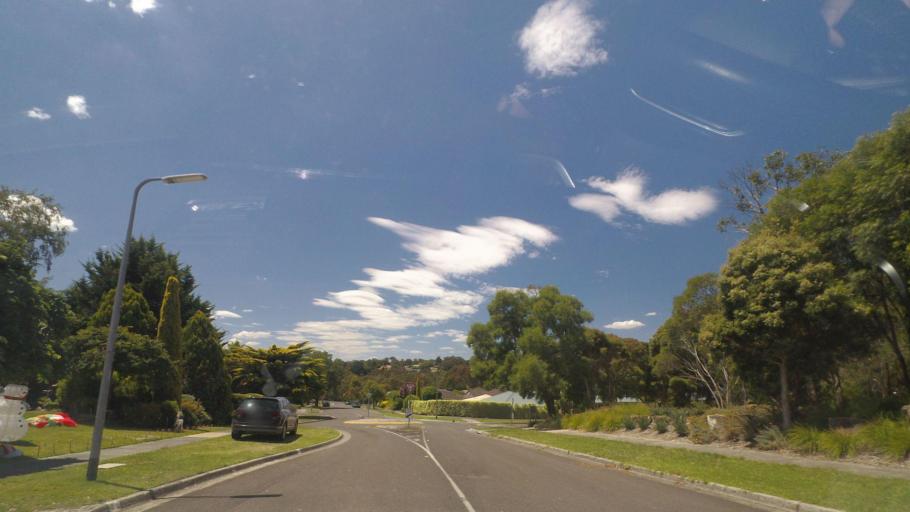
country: AU
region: Victoria
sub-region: Yarra Ranges
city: Kilsyth
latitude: -37.8035
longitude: 145.3334
